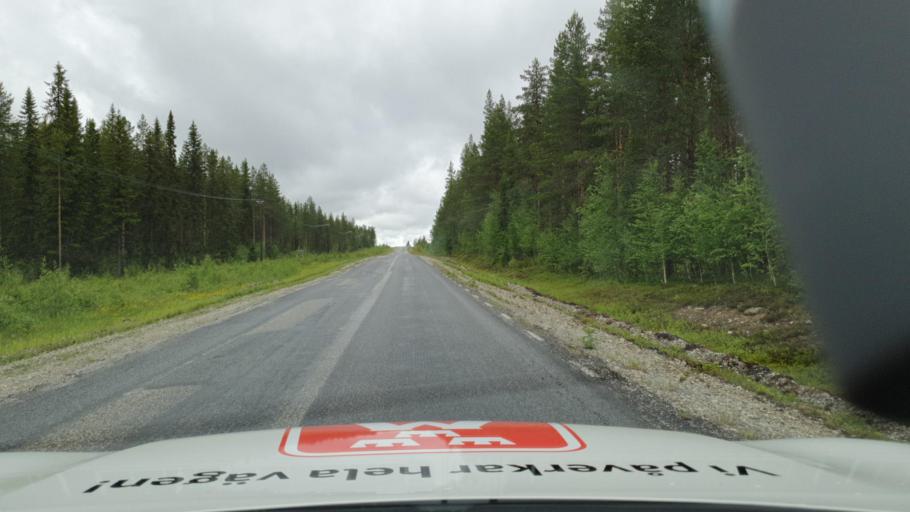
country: SE
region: Vaesterbotten
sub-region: Dorotea Kommun
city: Dorotea
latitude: 64.1593
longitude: 16.6493
